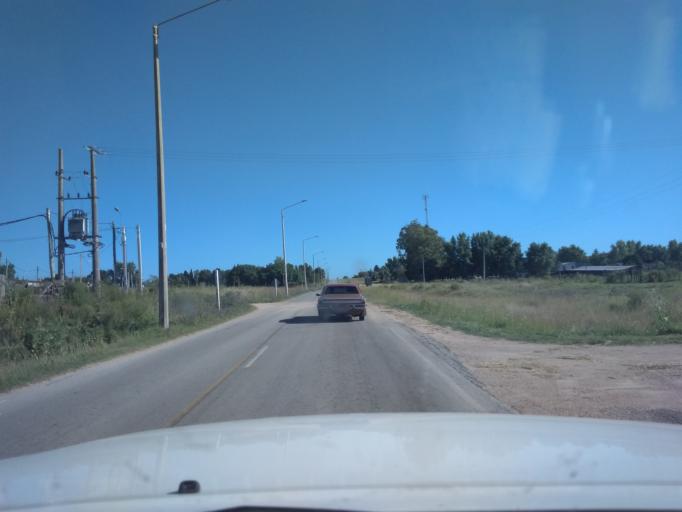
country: UY
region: Canelones
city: San Ramon
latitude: -34.3101
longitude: -55.9587
